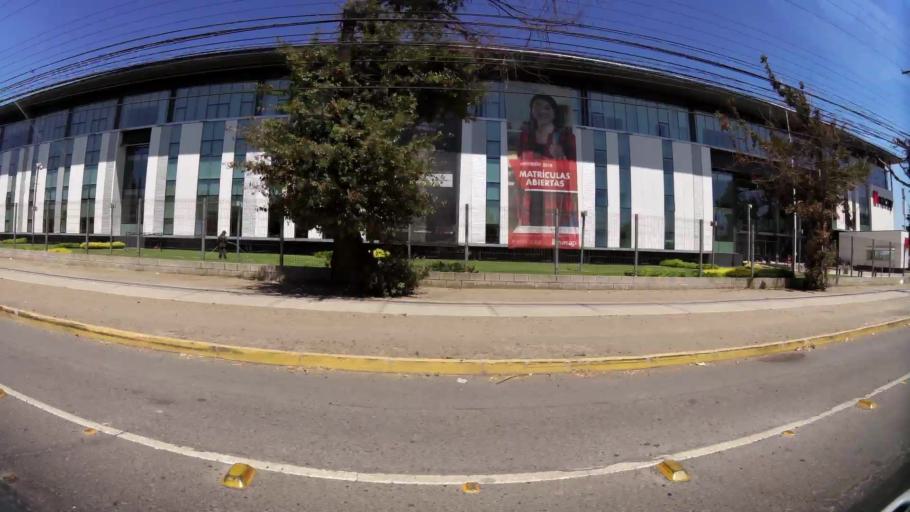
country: CL
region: Maule
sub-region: Provincia de Talca
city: Talca
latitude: -35.4364
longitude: -71.6236
